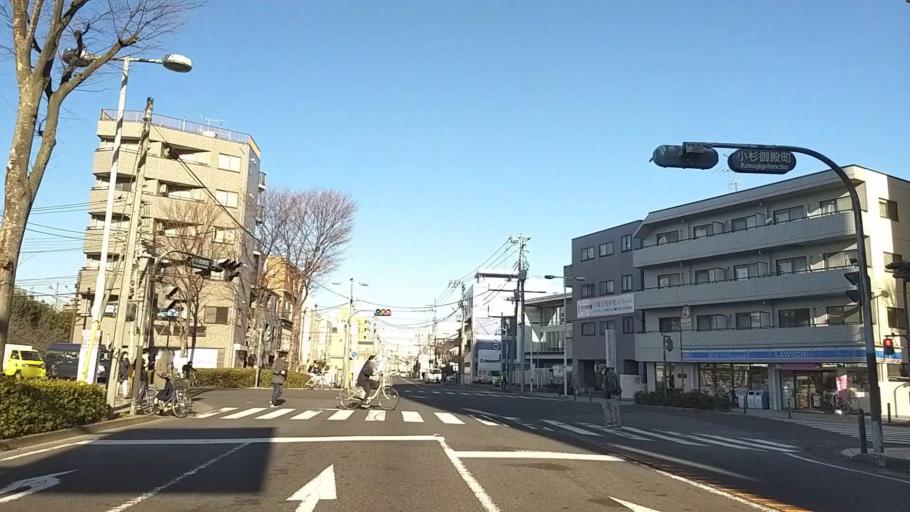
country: JP
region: Kanagawa
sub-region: Kawasaki-shi
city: Kawasaki
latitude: 35.5769
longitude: 139.6543
